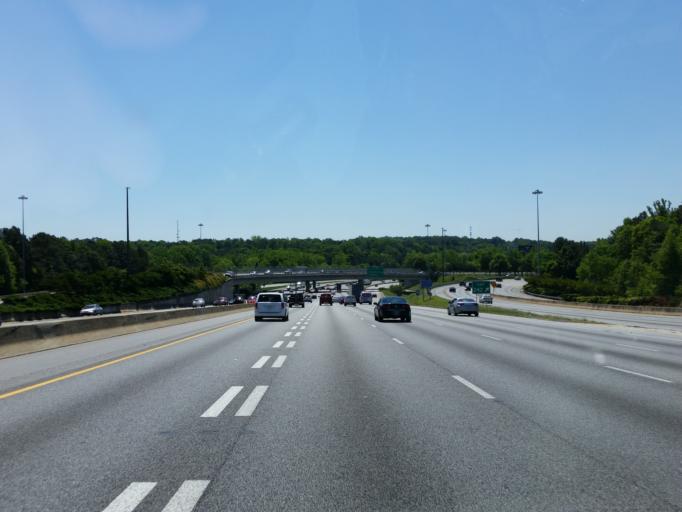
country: US
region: Georgia
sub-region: Fulton County
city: Hapeville
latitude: 33.6914
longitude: -84.4022
